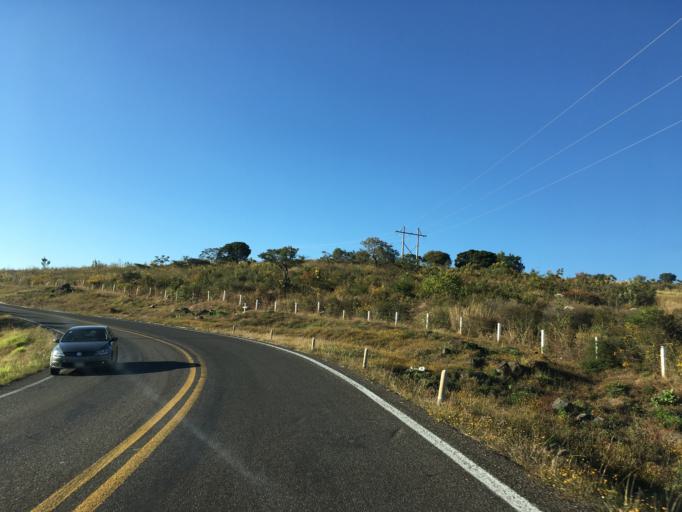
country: MX
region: Michoacan
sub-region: Tuxpan
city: La Soledad
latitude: 19.4906
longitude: -100.4495
